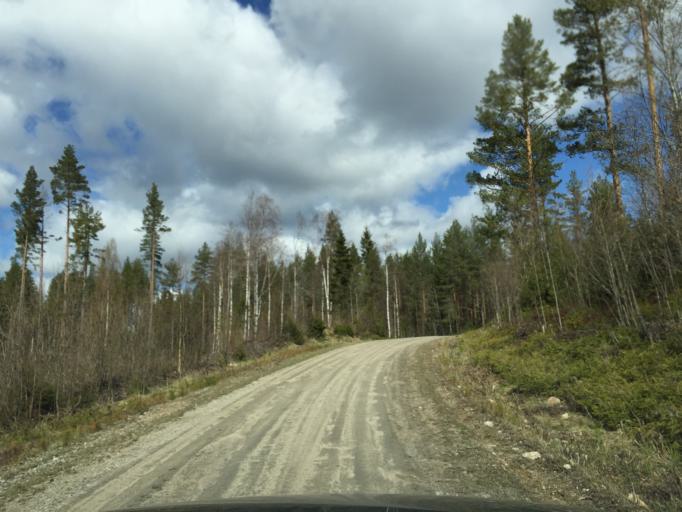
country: SE
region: Gaevleborg
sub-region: Bollnas Kommun
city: Arbra
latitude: 61.5218
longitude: 16.2898
